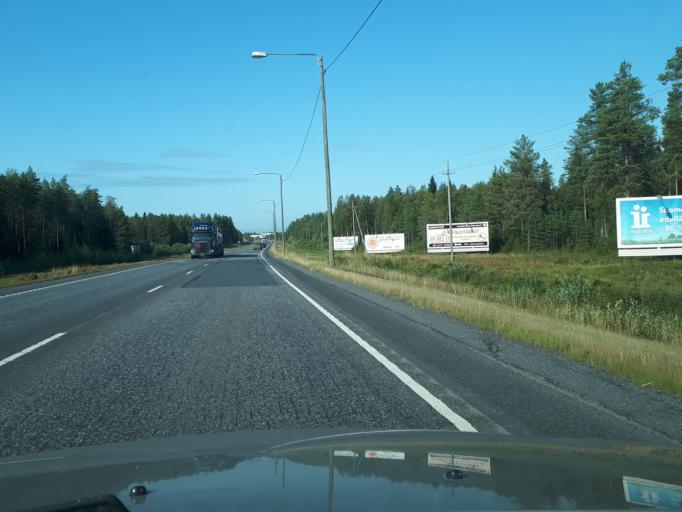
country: FI
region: Northern Ostrobothnia
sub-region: Oulunkaari
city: Ii
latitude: 65.2951
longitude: 25.3733
